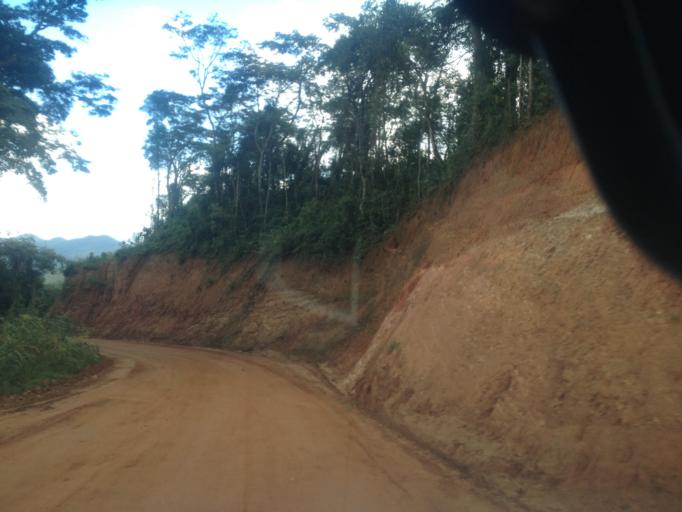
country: BR
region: Rio de Janeiro
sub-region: Quatis
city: Quatis
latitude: -22.2124
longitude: -44.2440
